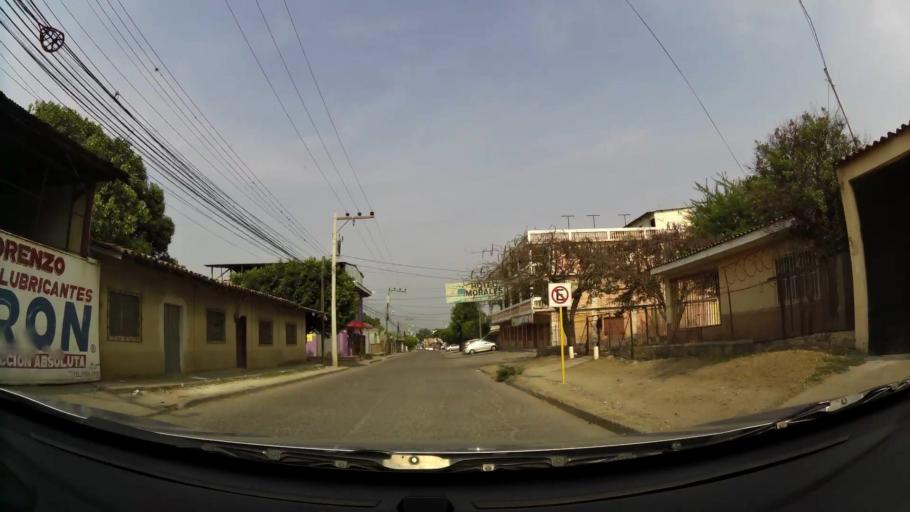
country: HN
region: Comayagua
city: Comayagua
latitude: 14.4567
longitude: -87.6340
